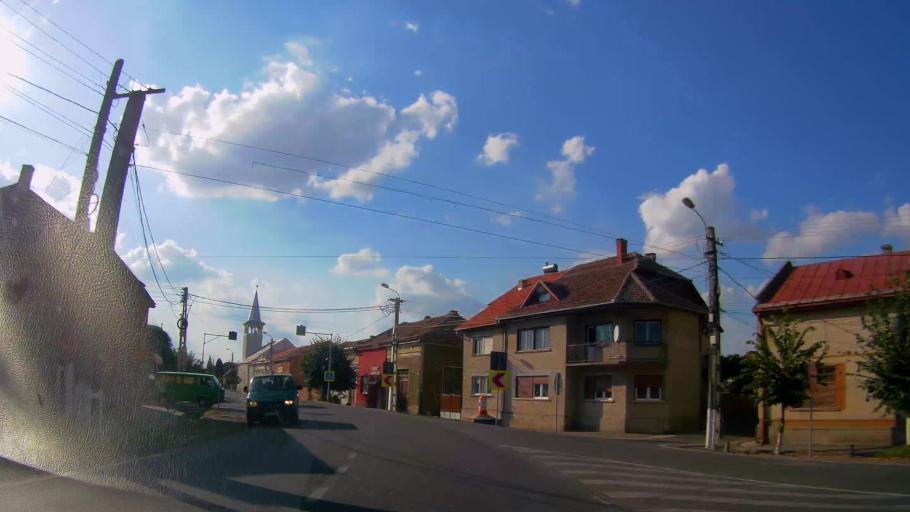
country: RO
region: Satu Mare
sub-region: Comuna Halmeu
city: Halmeu
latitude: 47.9772
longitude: 23.0170
